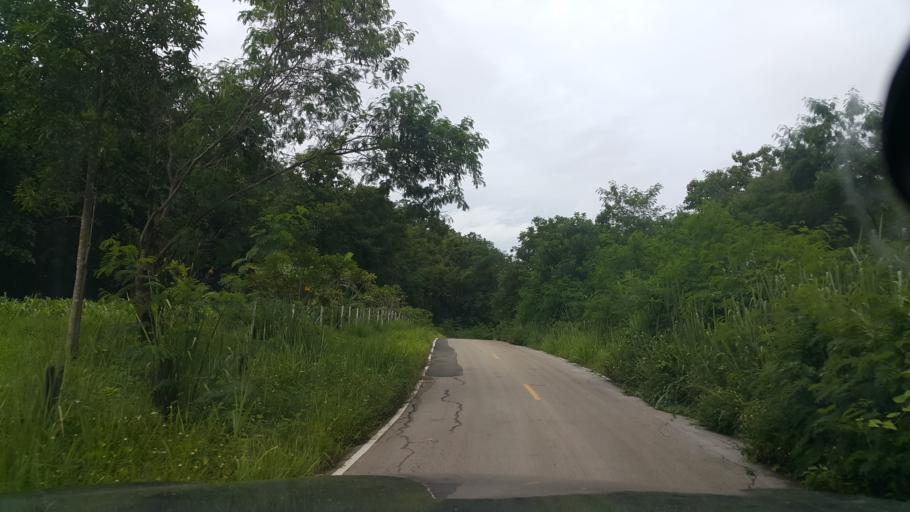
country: TH
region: Chiang Mai
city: Mae On
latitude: 18.8250
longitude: 99.2414
